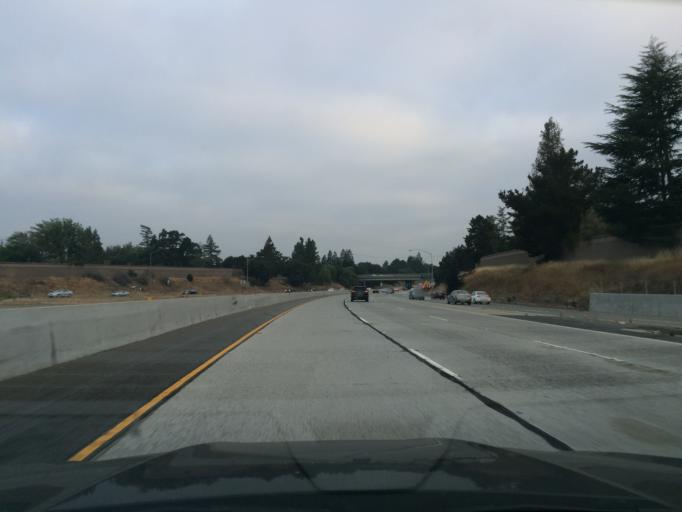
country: US
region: California
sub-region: Santa Clara County
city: Cupertino
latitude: 37.3346
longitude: -122.0579
